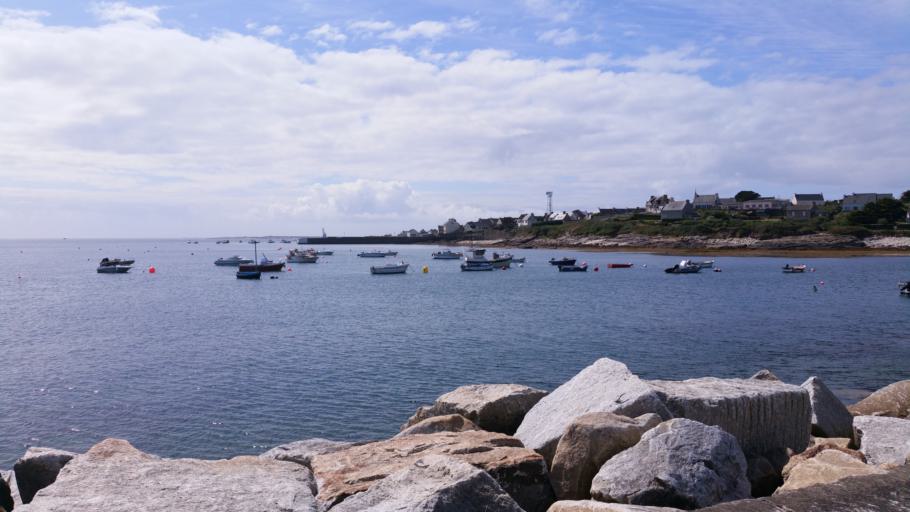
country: FR
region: Brittany
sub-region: Departement du Finistere
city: Le Conquet
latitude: 48.4018
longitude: -4.9576
